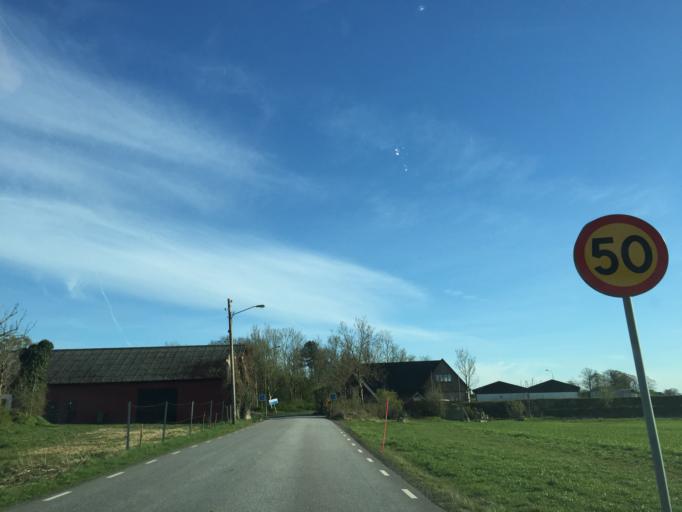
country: SE
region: Skane
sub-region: Malmo
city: Oxie
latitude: 55.5757
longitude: 13.0962
